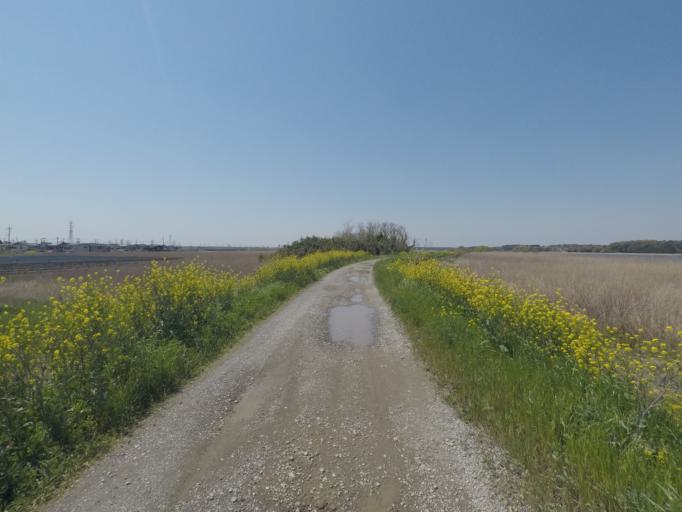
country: JP
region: Ibaraki
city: Fujishiro
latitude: 35.9405
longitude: 140.1241
